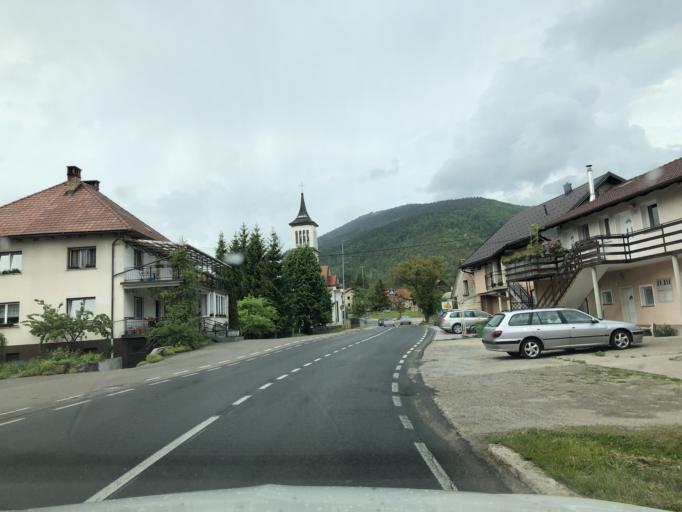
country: SI
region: Cerknica
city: Cerknica
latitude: 45.7695
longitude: 14.4250
